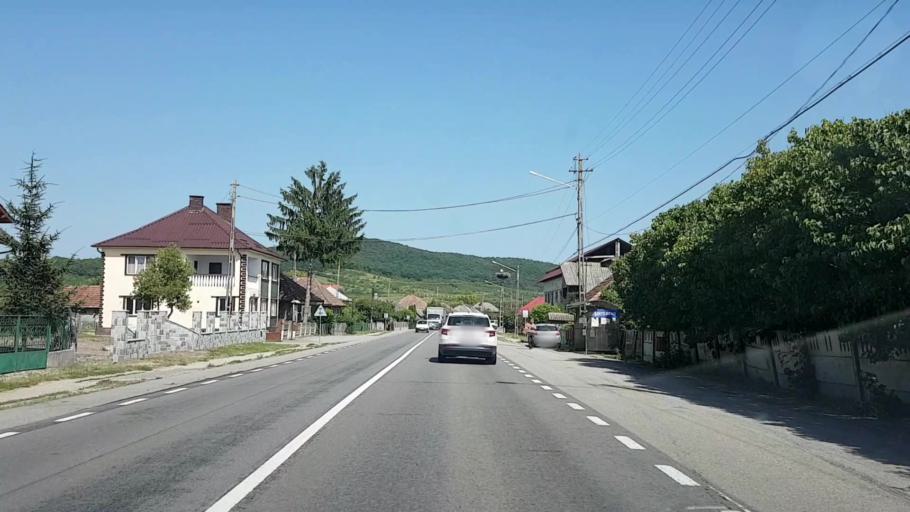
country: RO
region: Bistrita-Nasaud
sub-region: Comuna Sintereag
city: Sintereag
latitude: 47.1800
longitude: 24.2891
